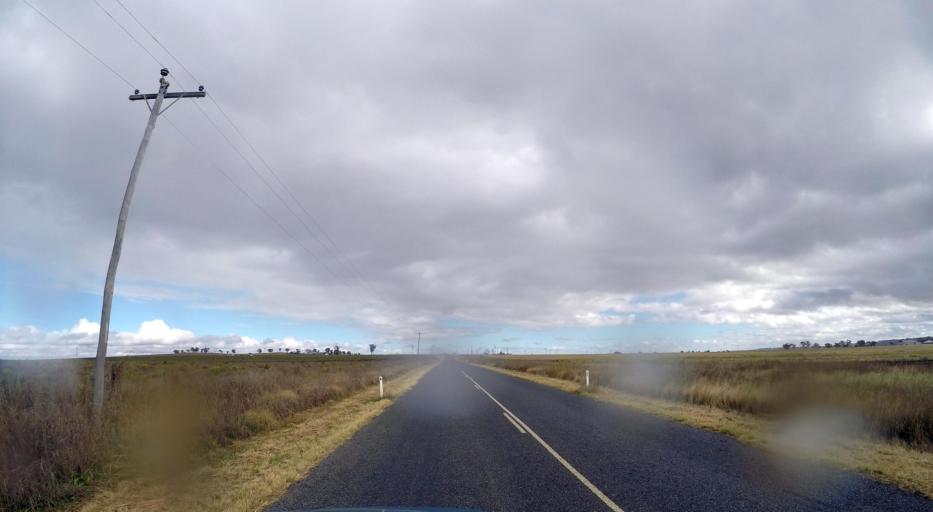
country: AU
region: Queensland
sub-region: Southern Downs
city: Warwick
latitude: -28.0560
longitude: 152.0211
